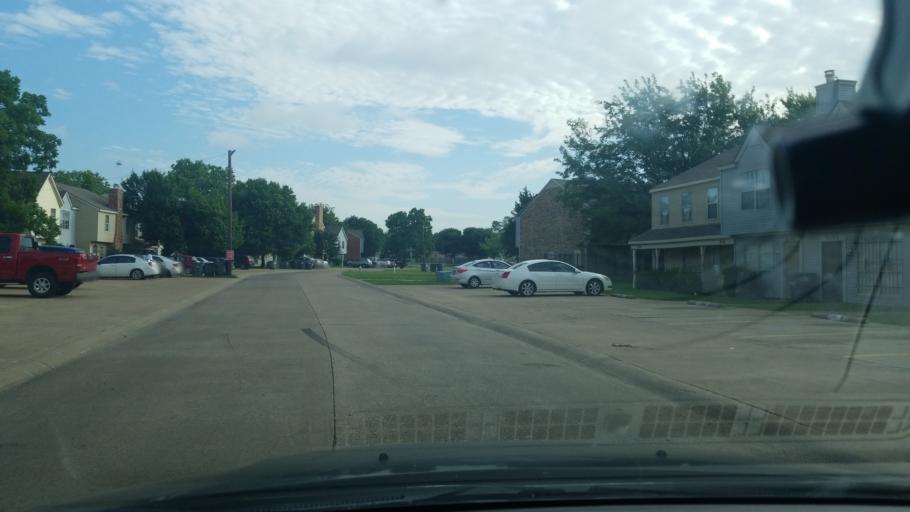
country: US
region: Texas
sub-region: Dallas County
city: Balch Springs
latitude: 32.7501
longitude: -96.6607
